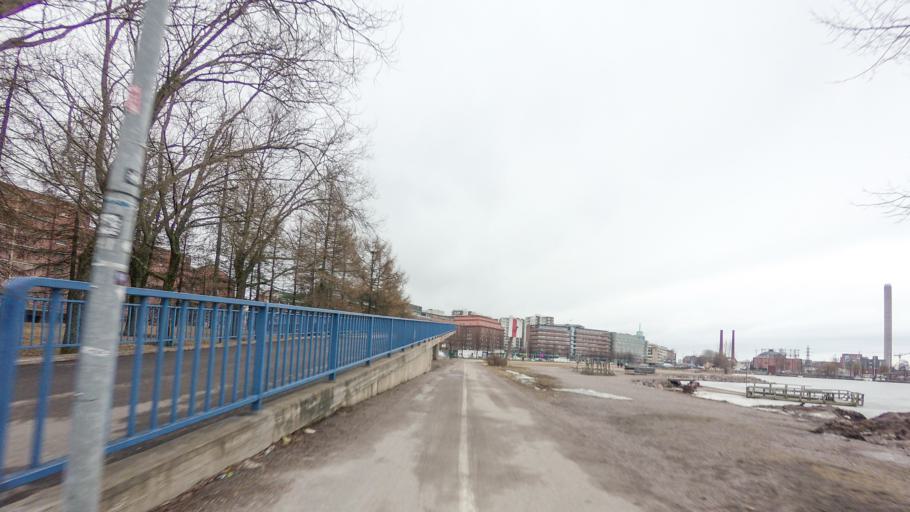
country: FI
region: Uusimaa
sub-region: Helsinki
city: Helsinki
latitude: 60.1812
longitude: 24.9621
